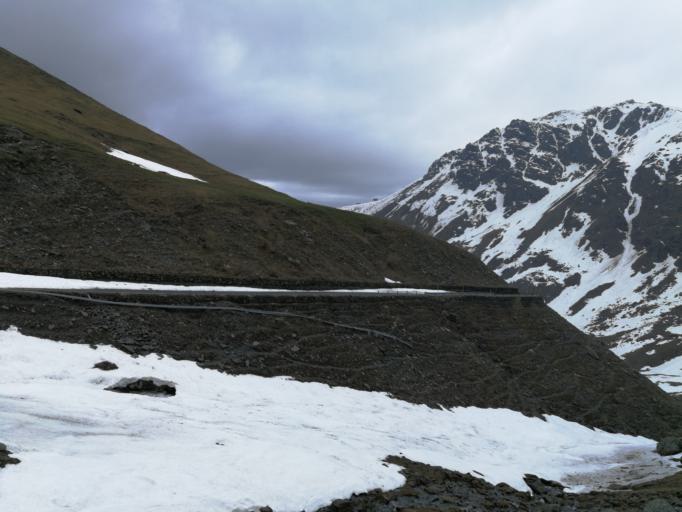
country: IT
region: Piedmont
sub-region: Provincia di Cuneo
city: Crissolo
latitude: 44.7042
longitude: 7.1095
